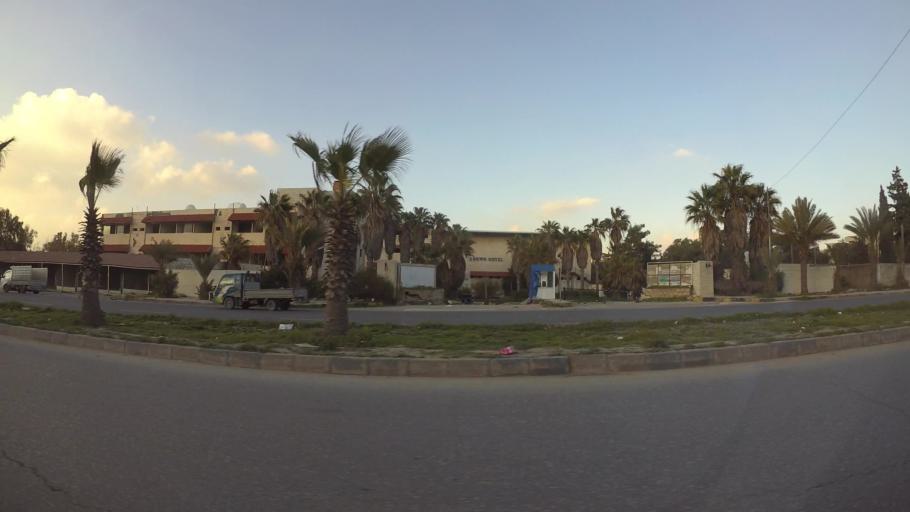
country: JO
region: Amman
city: Al Bunayyat ash Shamaliyah
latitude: 31.9132
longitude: 35.9177
